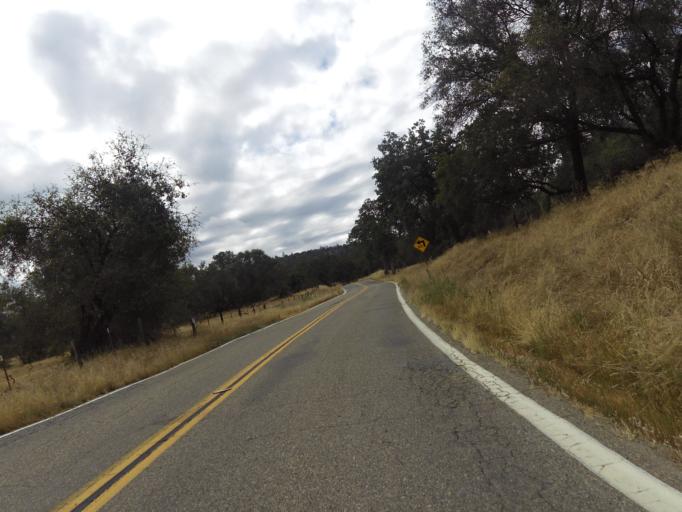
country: US
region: California
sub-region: Madera County
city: Yosemite Lakes
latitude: 37.2429
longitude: -119.8571
